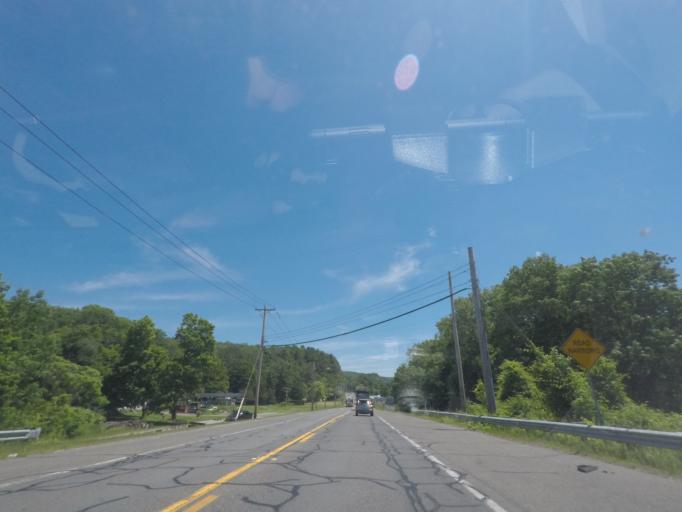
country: US
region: Massachusetts
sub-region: Berkshire County
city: Lee
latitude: 42.2965
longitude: -73.1837
